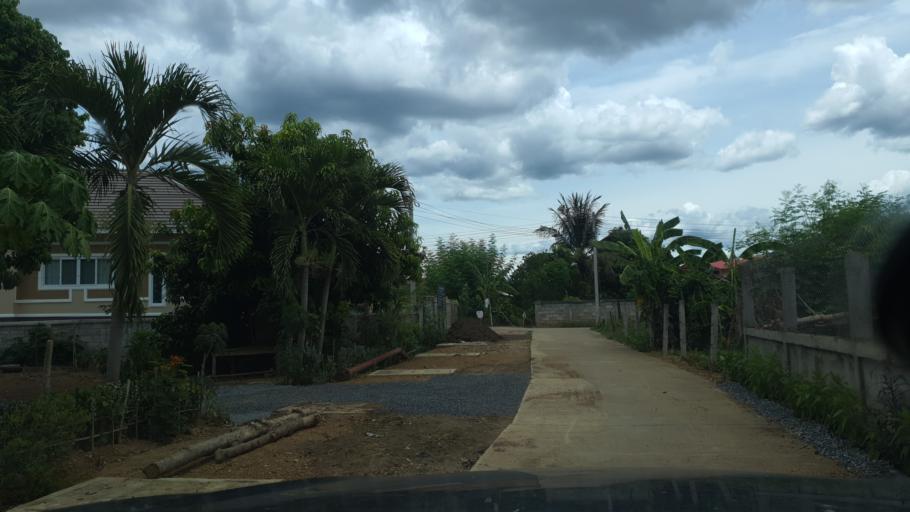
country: TH
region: Sukhothai
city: Thung Saliam
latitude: 17.3130
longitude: 99.5644
